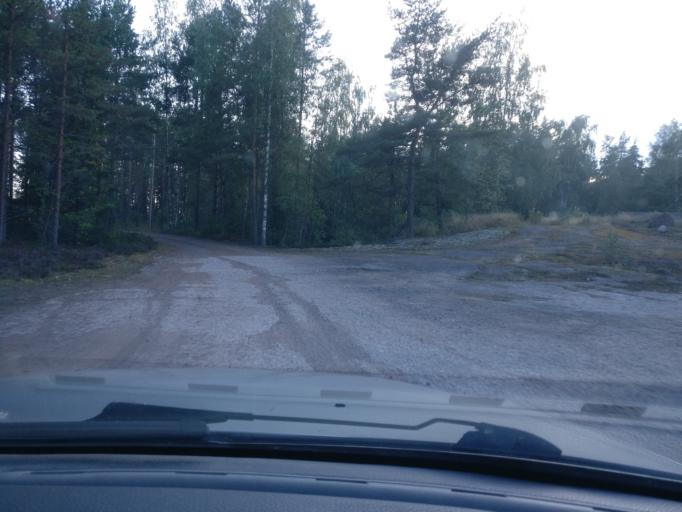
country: FI
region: Kymenlaakso
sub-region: Kotka-Hamina
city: Broby
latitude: 60.4716
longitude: 26.7746
